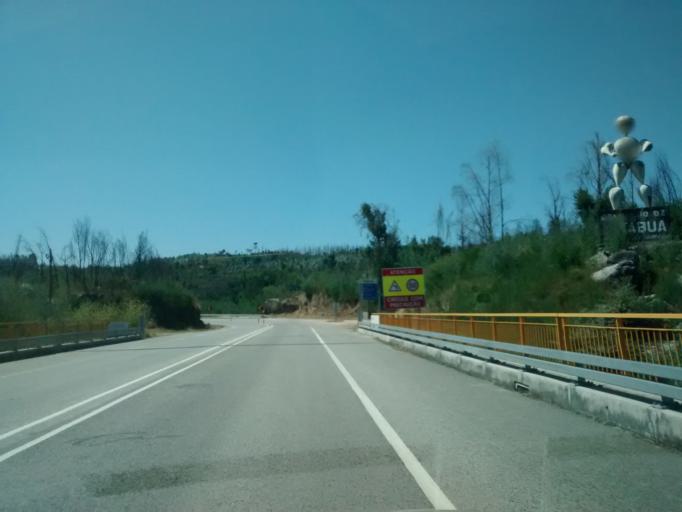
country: PT
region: Coimbra
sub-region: Tabua
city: Tabua
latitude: 40.3714
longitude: -8.0605
